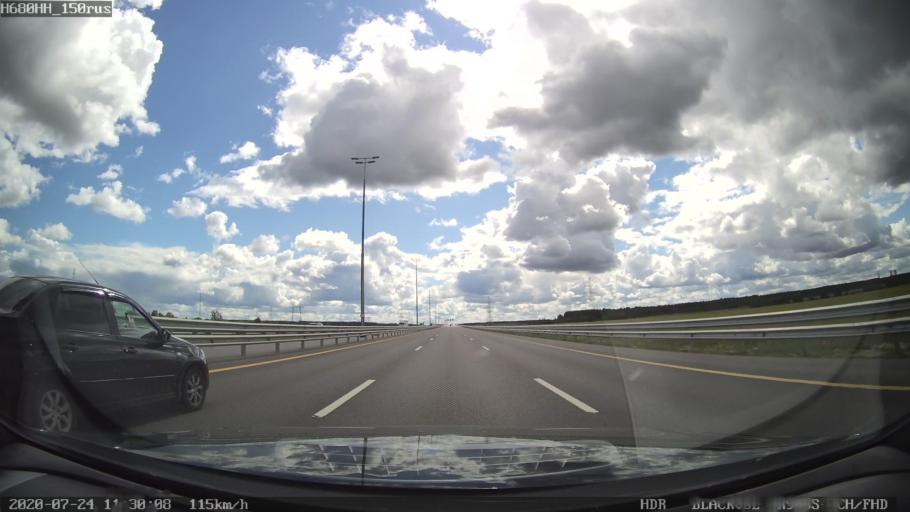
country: RU
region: Leningrad
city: Krasnyy Bor
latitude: 59.6729
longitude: 30.6063
